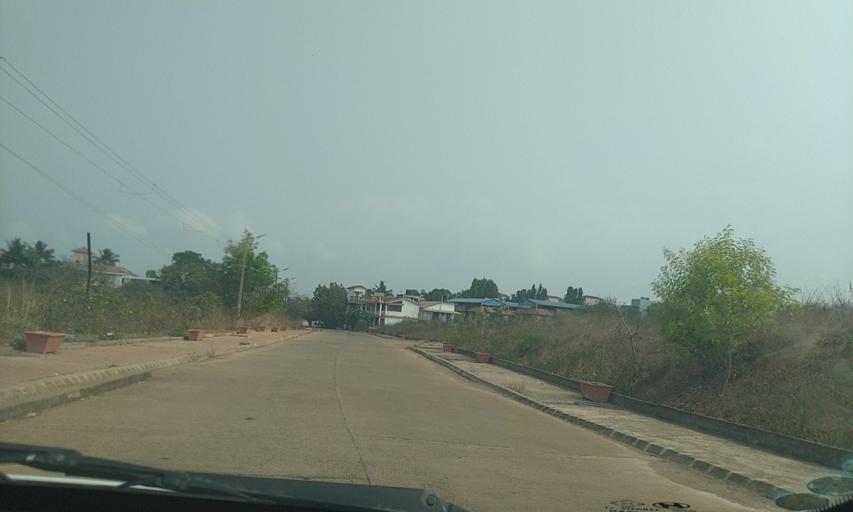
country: IN
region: Goa
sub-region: North Goa
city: Taleigao
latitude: 15.4610
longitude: 73.8174
